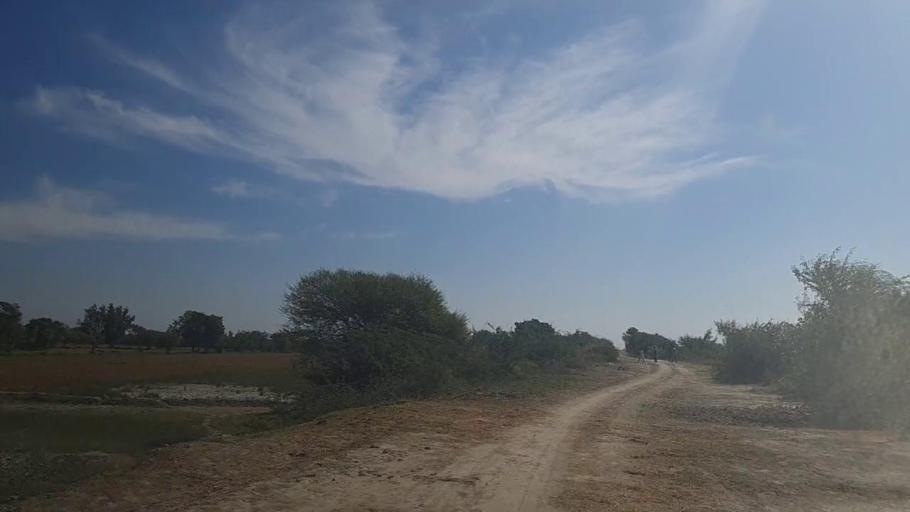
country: PK
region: Sindh
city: Mirpur Batoro
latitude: 24.6551
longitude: 68.2010
